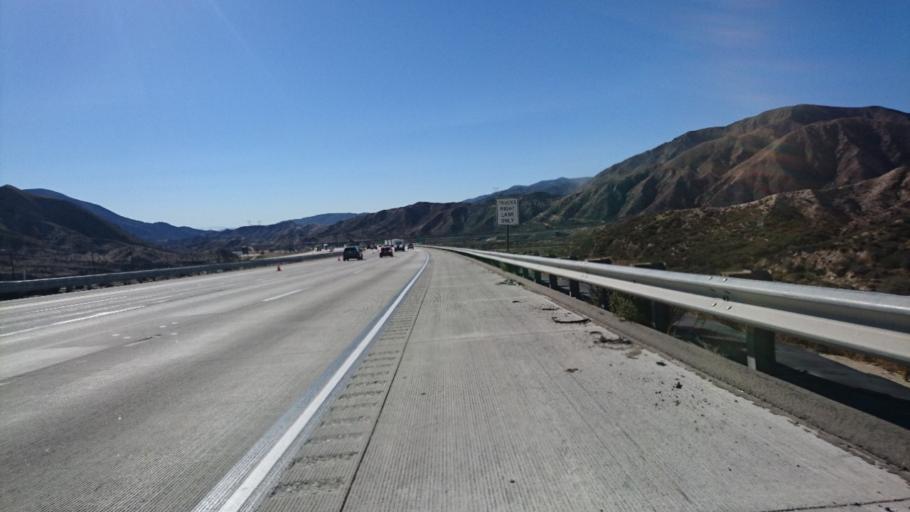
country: US
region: California
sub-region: San Bernardino County
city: Oak Hills
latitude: 34.3241
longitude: -117.4825
